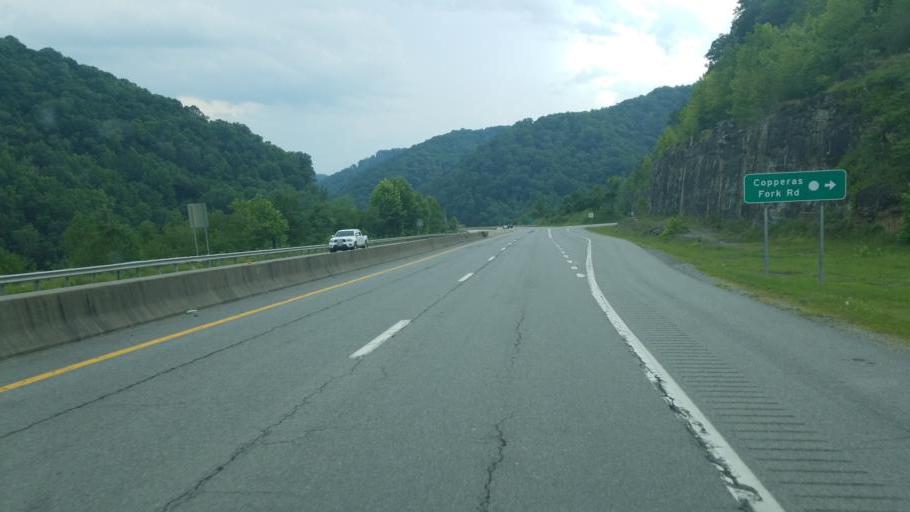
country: US
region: West Virginia
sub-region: Logan County
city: Mount Gay-Shamrock
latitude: 37.8274
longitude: -82.0527
